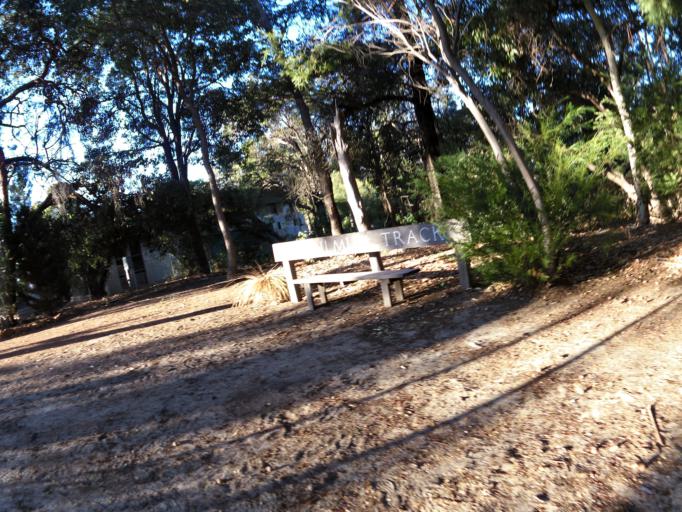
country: AU
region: Western Australia
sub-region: Kalamunda
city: Gooseberry Hill
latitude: -31.9730
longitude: 116.0604
